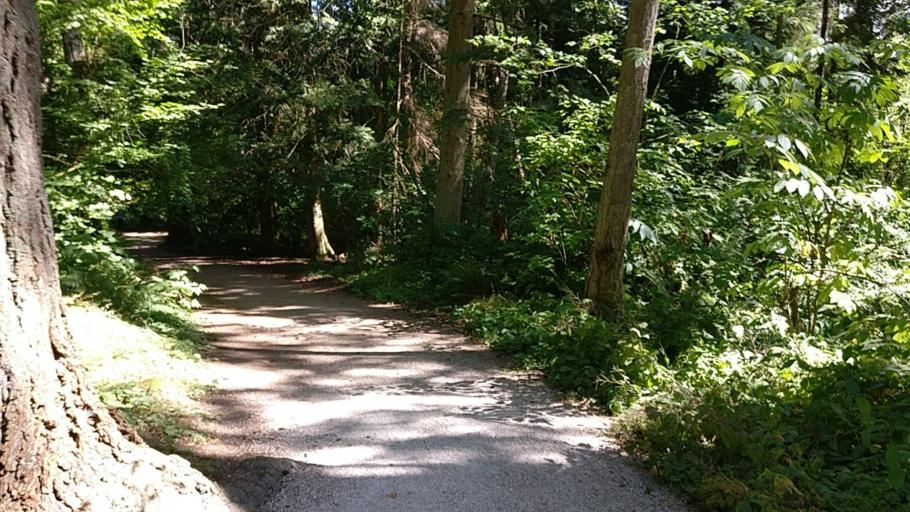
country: CA
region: British Columbia
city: Surrey
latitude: 49.0495
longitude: -122.8628
